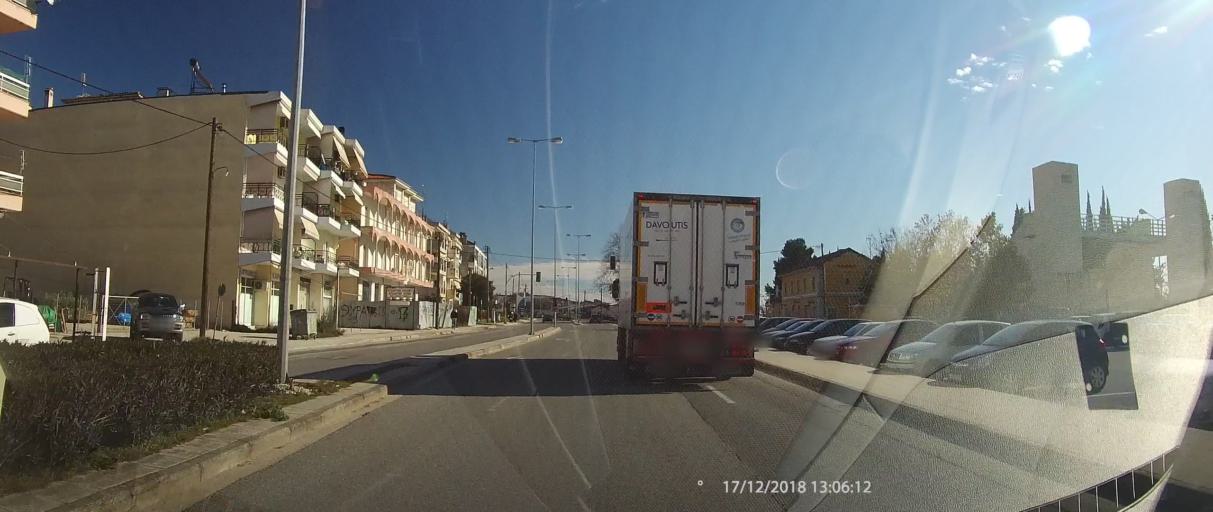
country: GR
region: Thessaly
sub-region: Trikala
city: Kalampaka
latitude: 39.7036
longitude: 21.6247
